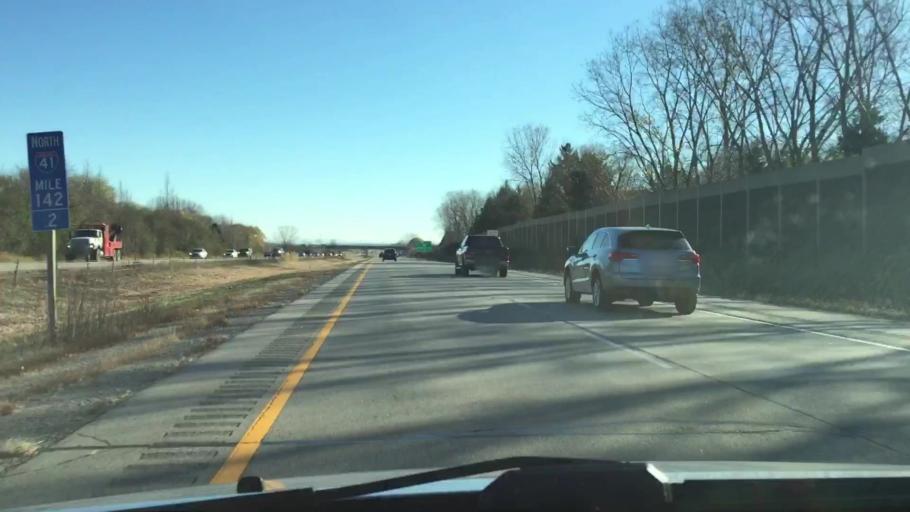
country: US
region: Wisconsin
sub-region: Outagamie County
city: Appleton
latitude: 44.2984
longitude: -88.4045
